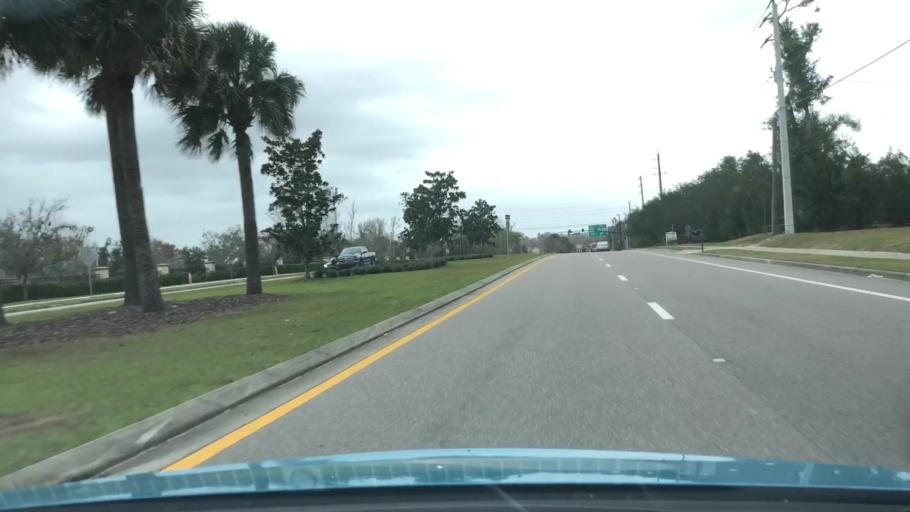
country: US
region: Florida
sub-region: Seminole County
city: Heathrow
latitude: 28.8065
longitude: -81.3479
